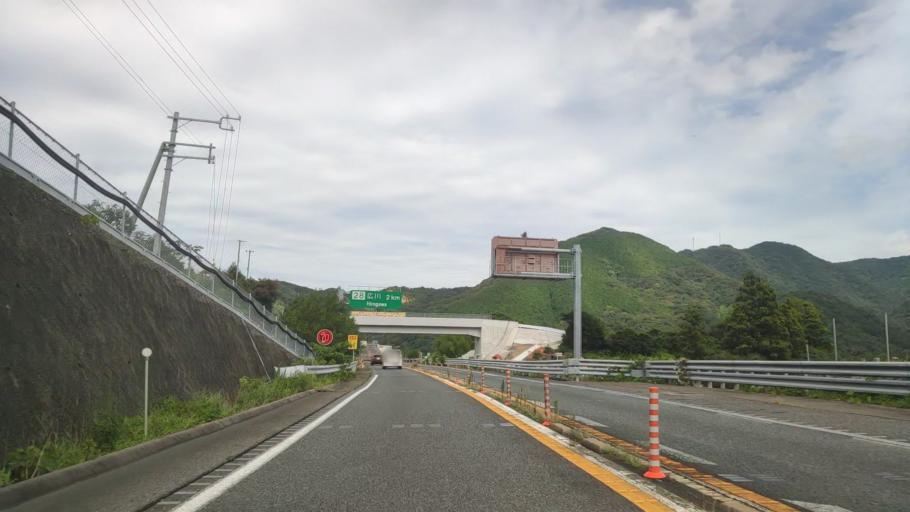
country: JP
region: Wakayama
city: Gobo
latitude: 33.9902
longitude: 135.1991
